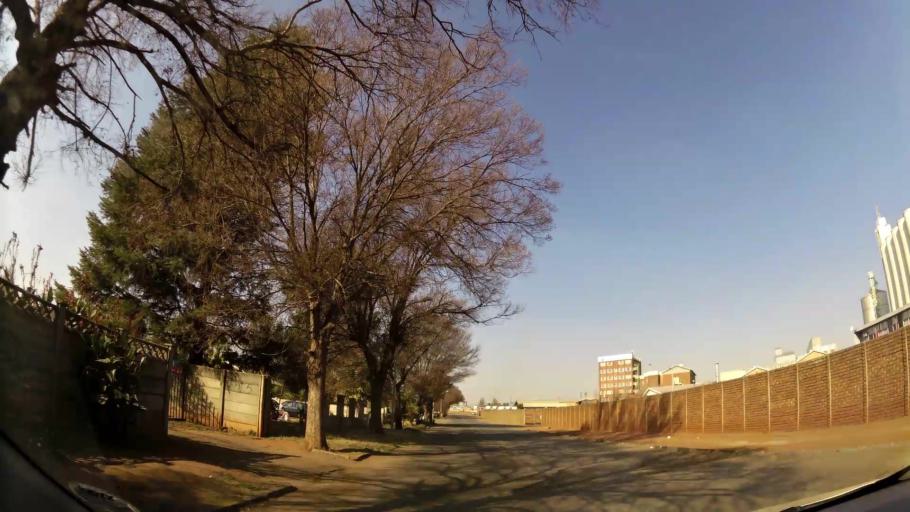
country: ZA
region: Gauteng
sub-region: West Rand District Municipality
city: Randfontein
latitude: -26.1846
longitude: 27.6918
